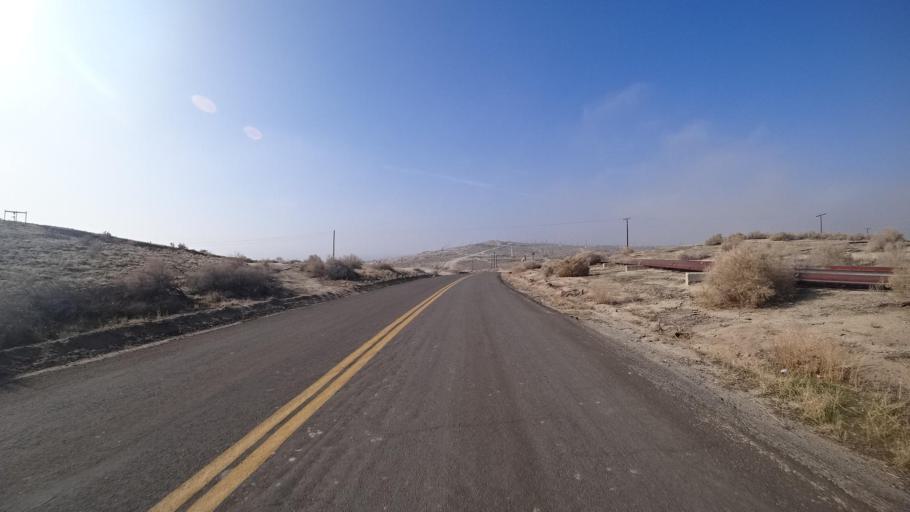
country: US
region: California
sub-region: Kern County
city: Ford City
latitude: 35.1636
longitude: -119.4175
